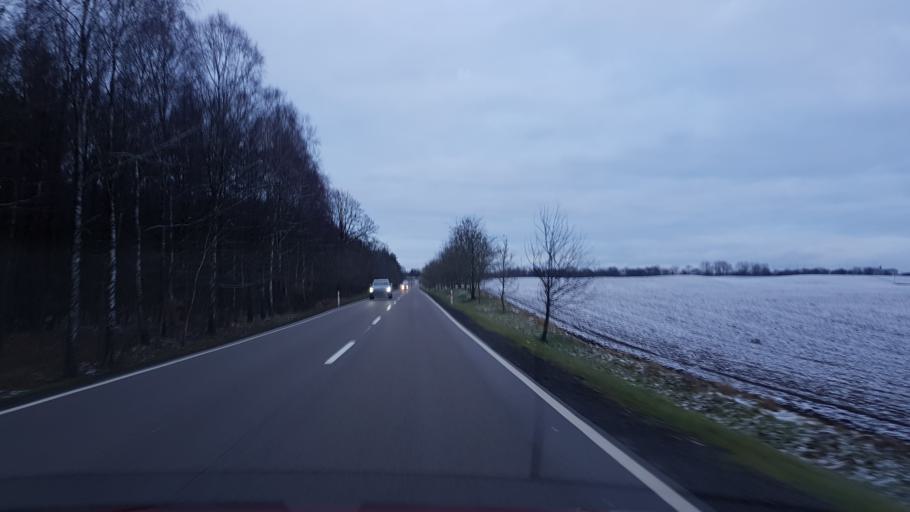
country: PL
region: Pomeranian Voivodeship
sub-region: Powiat czluchowski
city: Koczala
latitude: 54.0195
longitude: 17.1470
